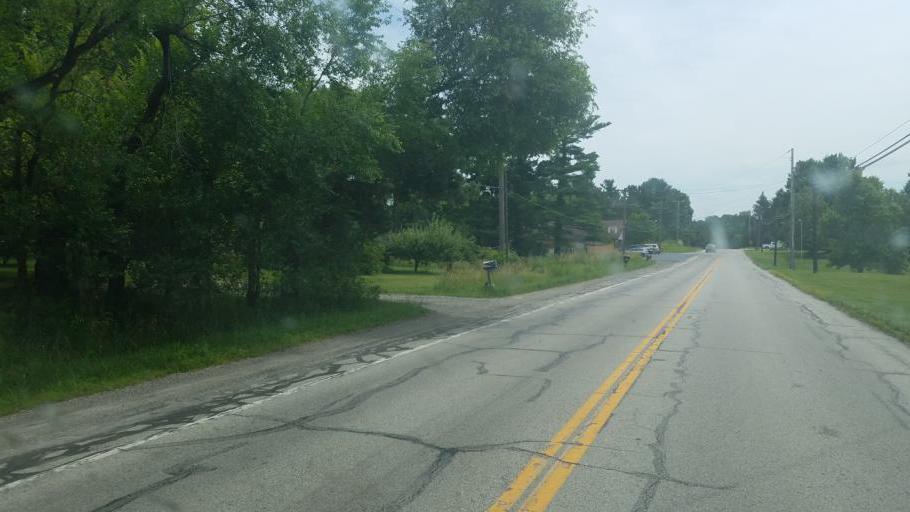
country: US
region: Ohio
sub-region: Geauga County
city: Bainbridge
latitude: 41.3877
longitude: -81.2636
